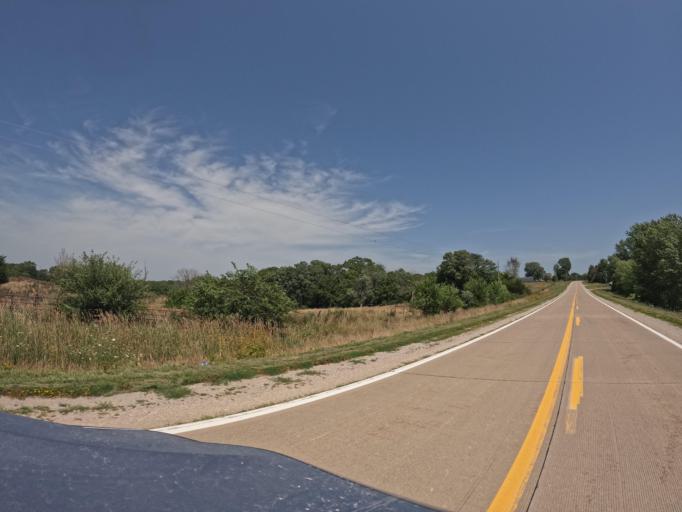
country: US
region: Iowa
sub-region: Henry County
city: Mount Pleasant
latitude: 40.9875
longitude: -91.6452
